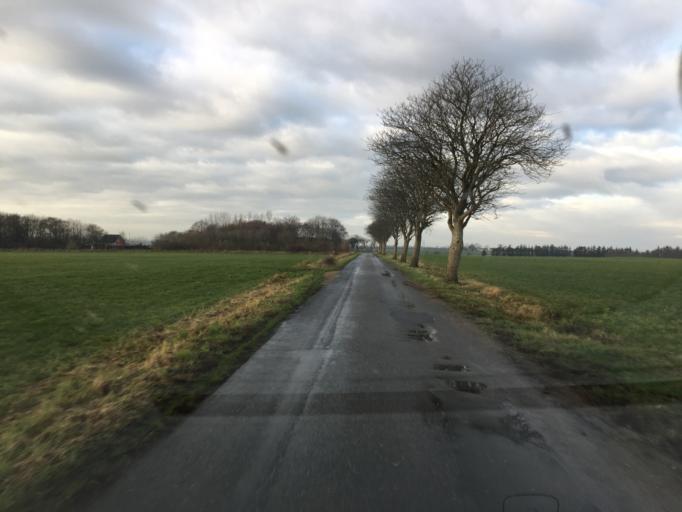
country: DK
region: South Denmark
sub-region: Tonder Kommune
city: Logumkloster
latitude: 55.1149
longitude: 8.8731
